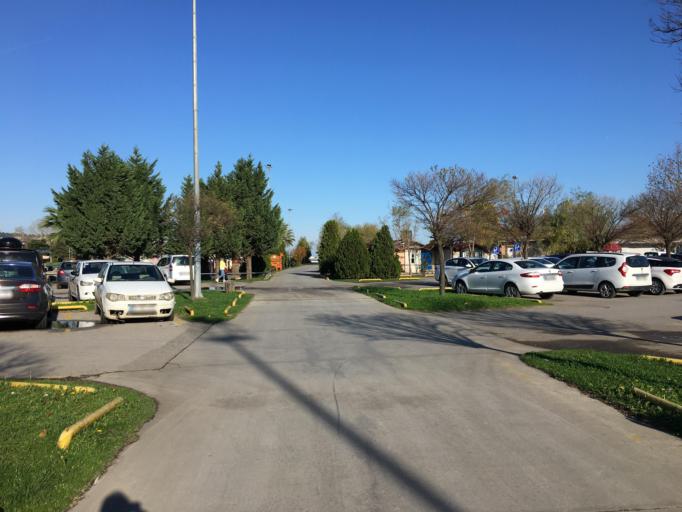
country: TR
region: Samsun
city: Samsun
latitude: 41.2853
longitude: 36.3456
